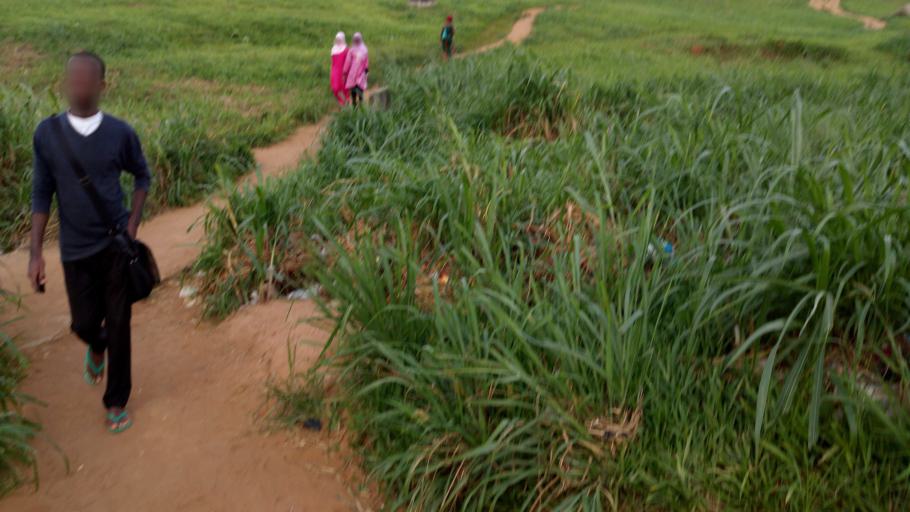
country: CI
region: Lagunes
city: Abidjan
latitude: 5.3430
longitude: -3.9914
